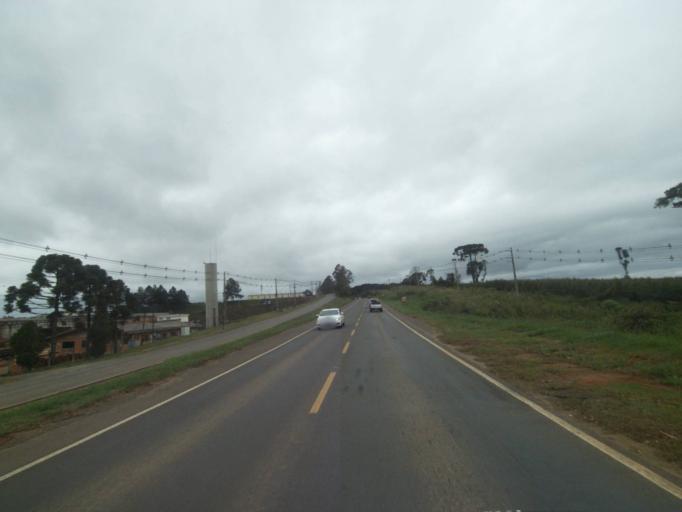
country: BR
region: Parana
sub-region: Telemaco Borba
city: Telemaco Borba
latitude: -24.3713
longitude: -50.6619
